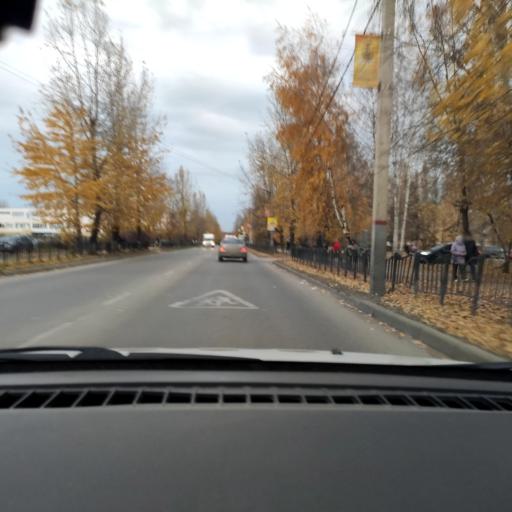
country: RU
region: Perm
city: Perm
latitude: 58.1076
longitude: 56.3799
